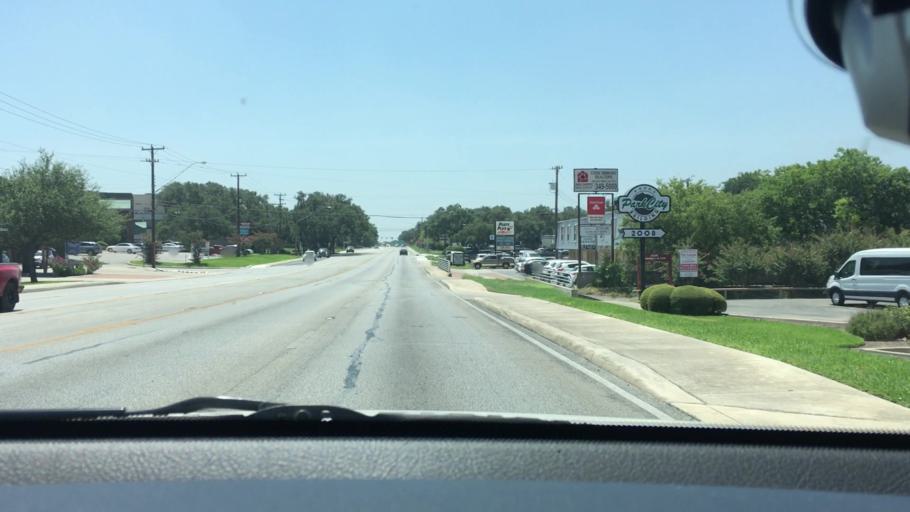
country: US
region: Texas
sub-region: Bexar County
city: Castle Hills
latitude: 29.5296
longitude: -98.5203
